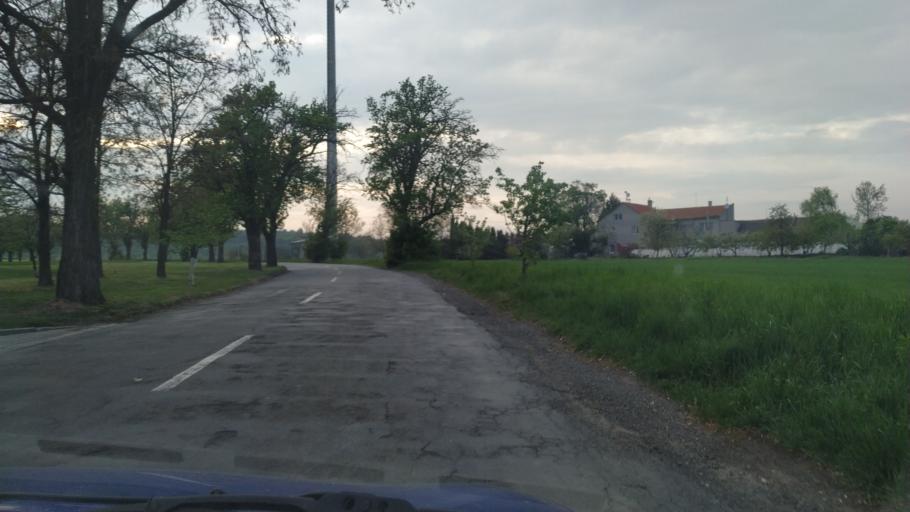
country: CZ
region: Olomoucky
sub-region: Okres Olomouc
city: Slatinice
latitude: 49.5523
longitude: 17.1063
